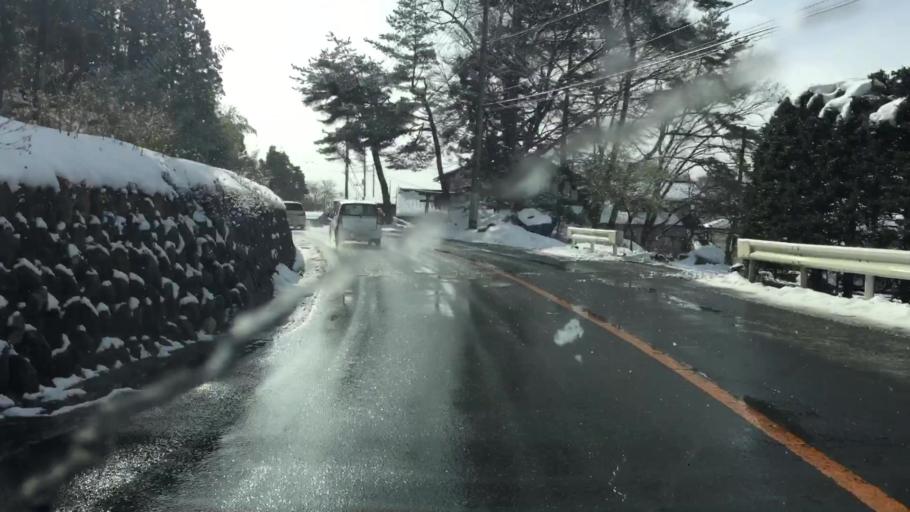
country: JP
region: Gunma
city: Numata
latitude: 36.6734
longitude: 139.0628
